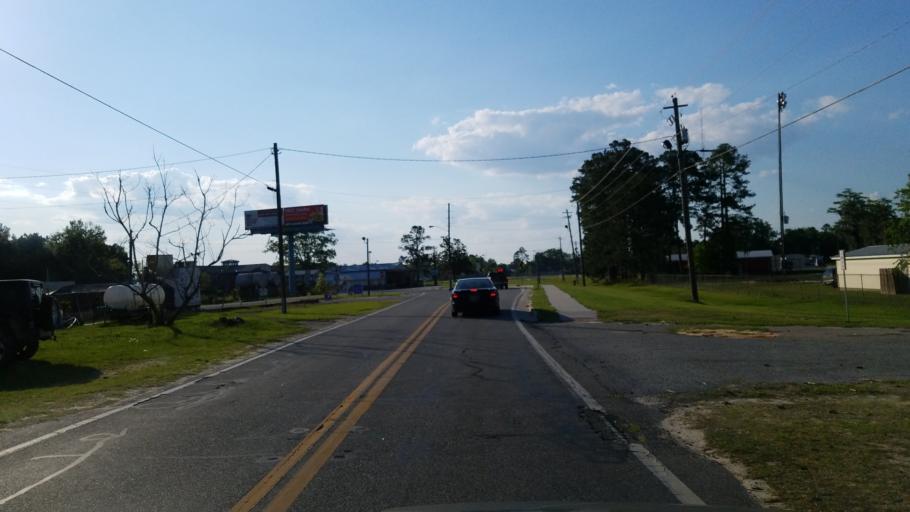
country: US
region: Georgia
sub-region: Lanier County
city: Lakeland
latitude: 31.0325
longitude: -83.0715
